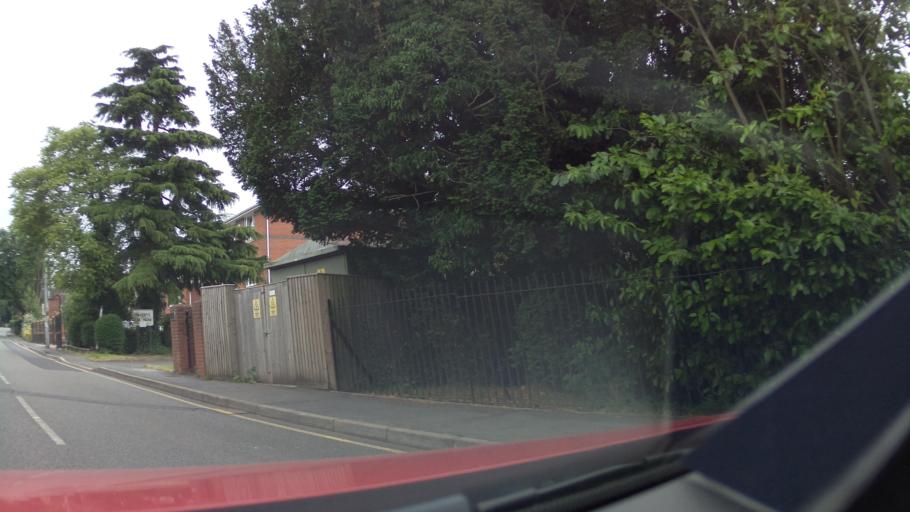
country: GB
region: England
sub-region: Leicestershire
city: Melton Mowbray
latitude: 52.7599
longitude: -0.8894
